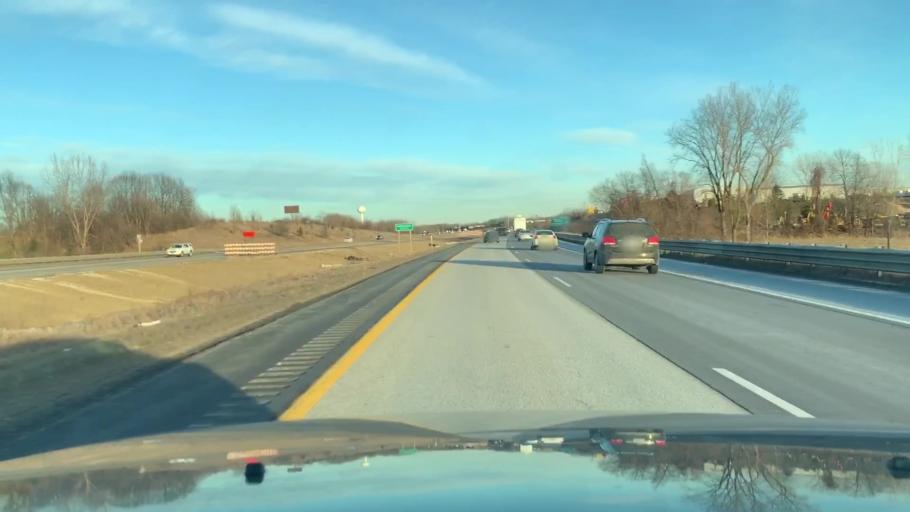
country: US
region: Michigan
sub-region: Ottawa County
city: Hudsonville
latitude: 42.8472
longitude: -85.8735
